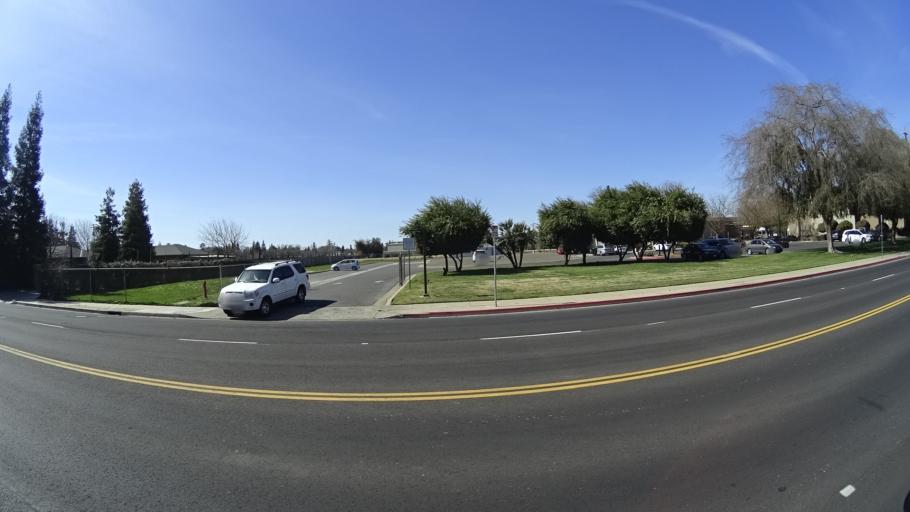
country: US
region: California
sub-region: Fresno County
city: Fresno
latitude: 36.7995
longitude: -119.8085
